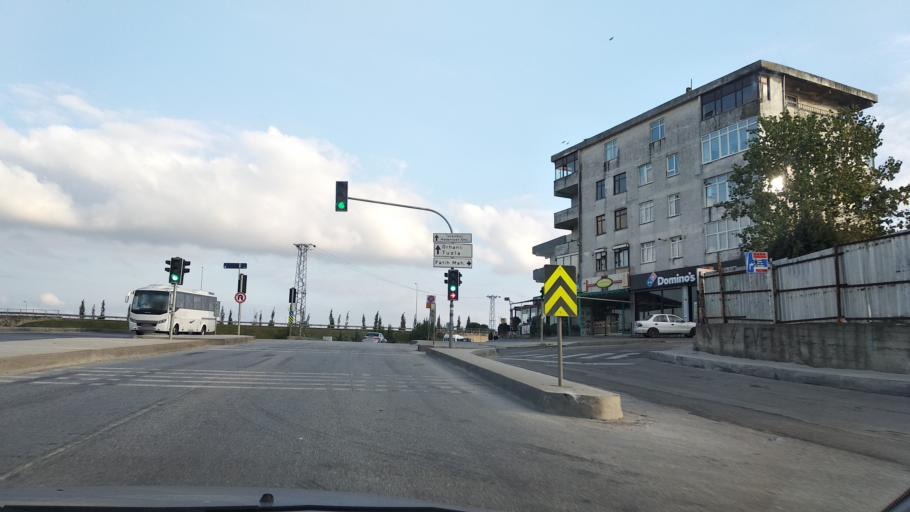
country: TR
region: Istanbul
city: Sultanbeyli
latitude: 40.9300
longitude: 29.3431
